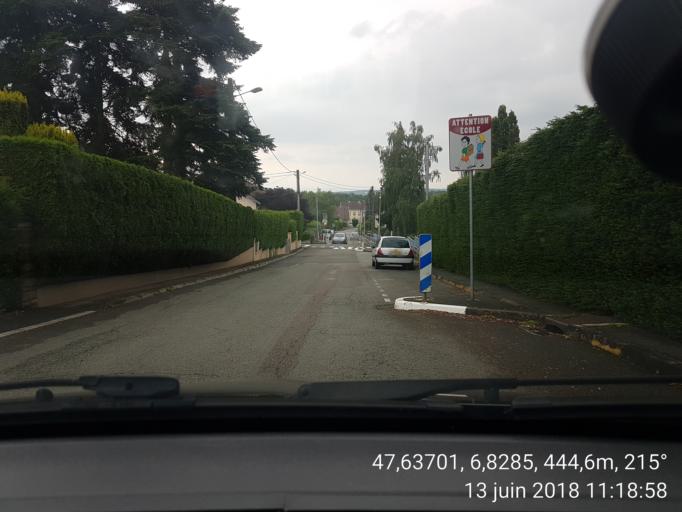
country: FR
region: Franche-Comte
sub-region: Territoire de Belfort
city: Essert
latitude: 47.6370
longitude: 6.8285
